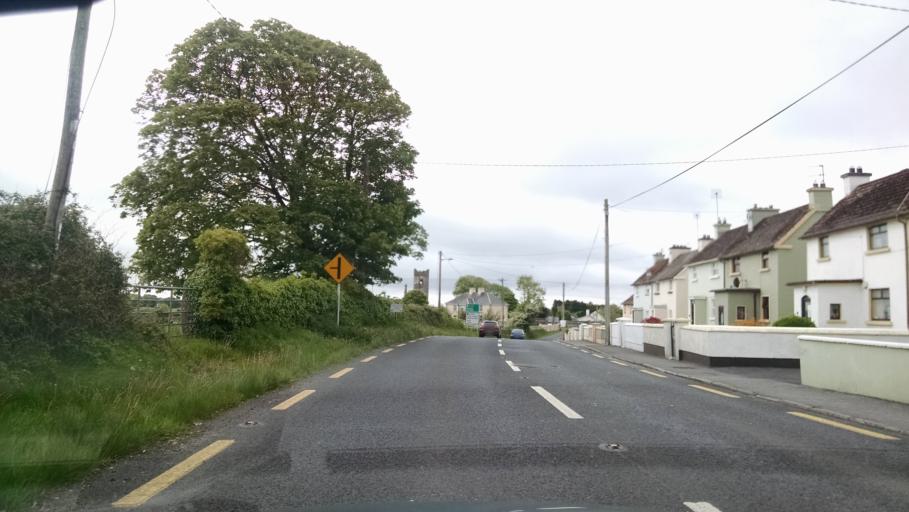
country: IE
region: Connaught
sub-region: County Galway
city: Moycullen
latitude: 53.4759
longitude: -9.0935
